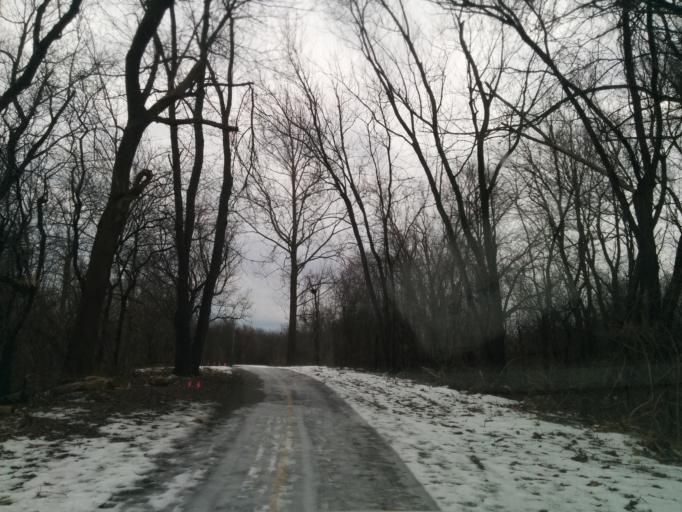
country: US
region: Illinois
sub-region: Cook County
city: Glencoe
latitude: 42.1338
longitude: -87.7804
